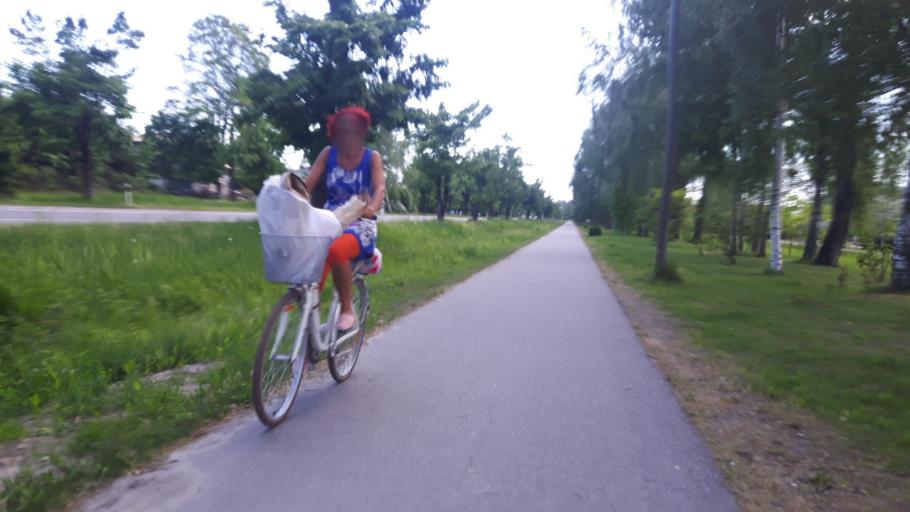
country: EE
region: Paernumaa
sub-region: Paikuse vald
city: Paikuse
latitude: 58.3793
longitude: 24.6285
